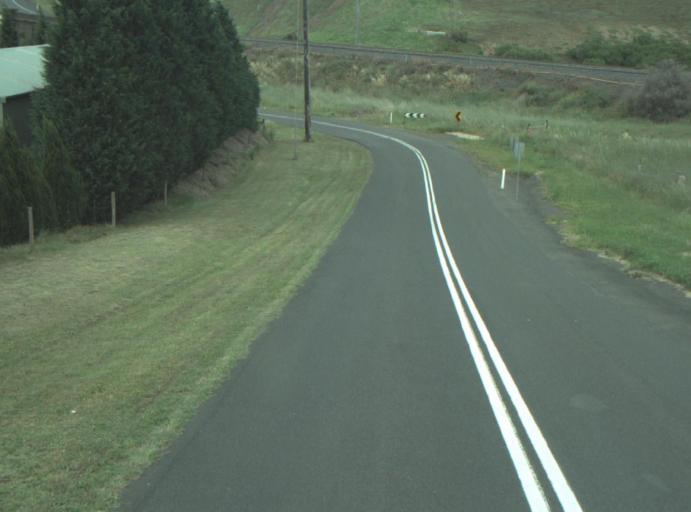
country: AU
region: Victoria
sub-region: Greater Geelong
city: Bell Post Hill
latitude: -38.0863
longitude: 144.3257
